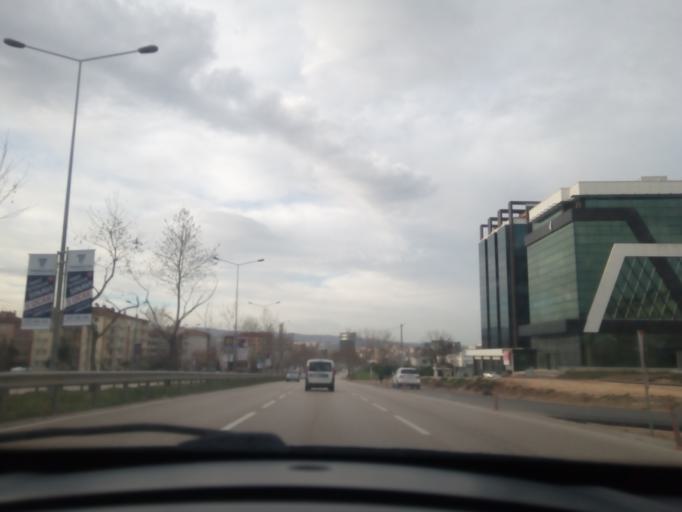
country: TR
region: Bursa
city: Niluefer
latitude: 40.2260
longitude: 28.9602
